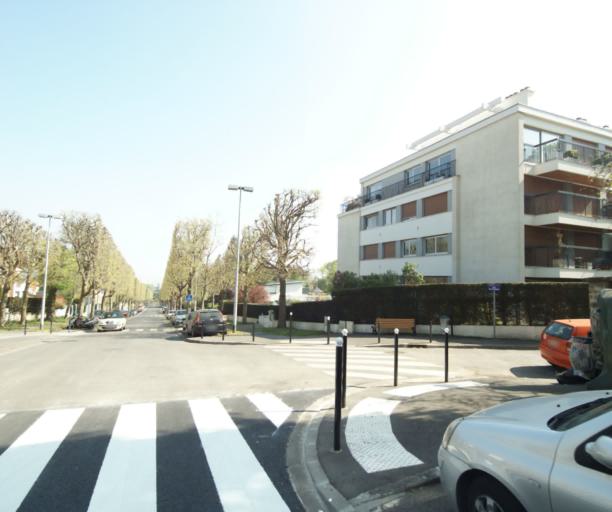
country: FR
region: Ile-de-France
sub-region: Departement des Hauts-de-Seine
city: Sevres
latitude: 48.8169
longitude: 2.2201
